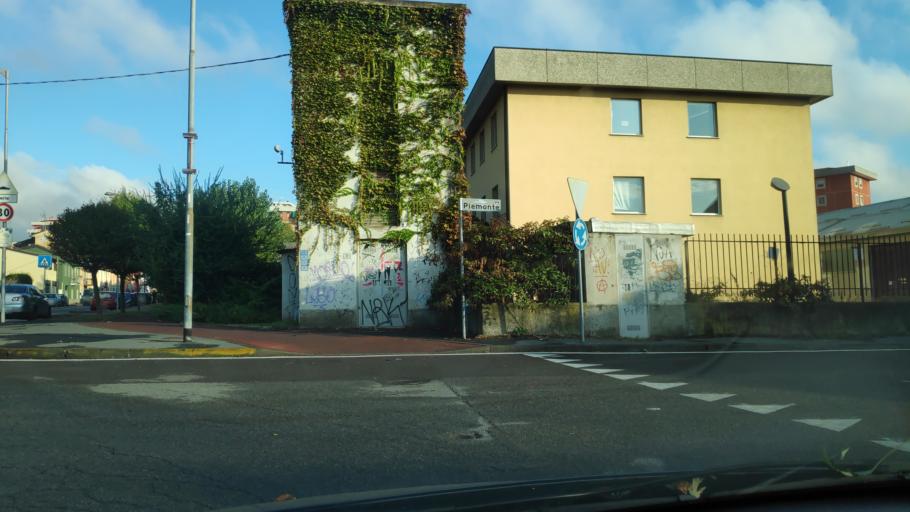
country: IT
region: Lombardy
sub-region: Citta metropolitana di Milano
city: Opera
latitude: 45.3720
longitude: 9.2135
